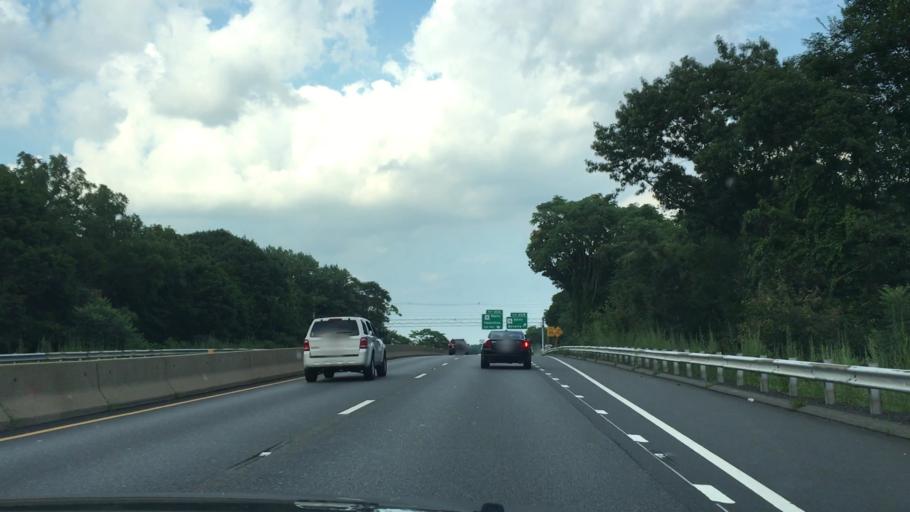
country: US
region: Massachusetts
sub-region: Essex County
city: Beverly
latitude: 42.5740
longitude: -70.8966
